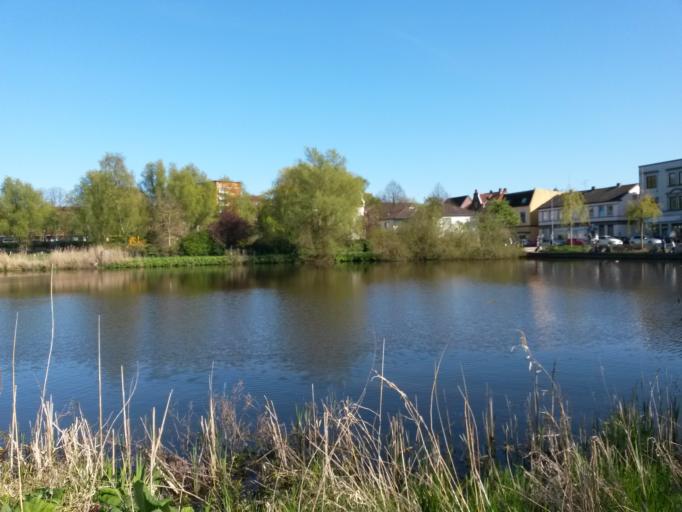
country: DE
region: Schleswig-Holstein
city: Wedel
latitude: 53.5824
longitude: 9.7017
